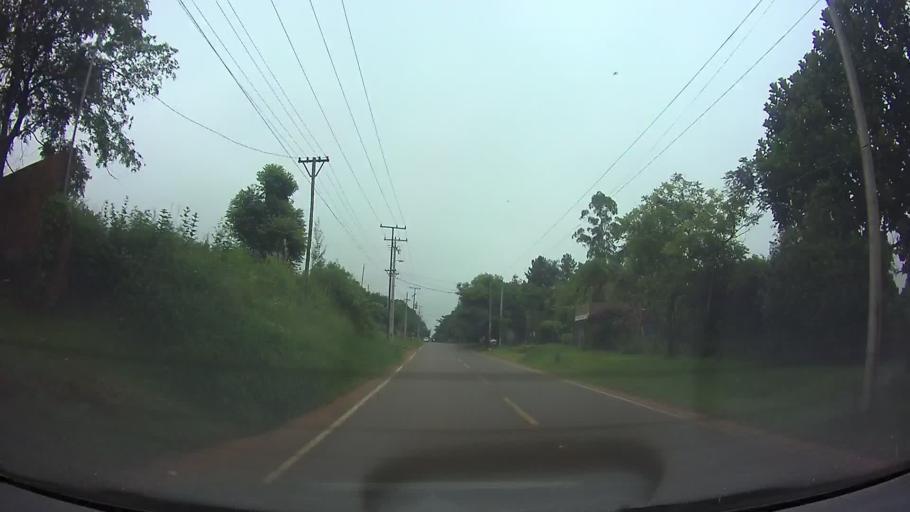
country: PY
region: Central
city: Itaugua
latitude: -25.3792
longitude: -57.3495
